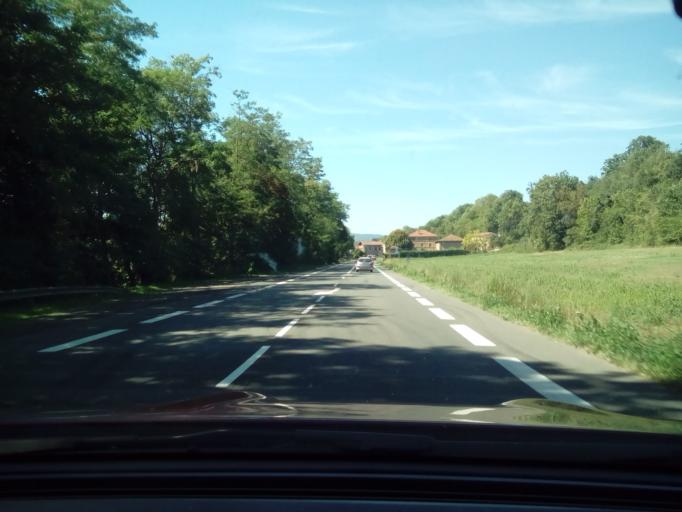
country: FR
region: Rhone-Alpes
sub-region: Departement du Rhone
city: Chatillon
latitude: 45.8928
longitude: 4.5983
